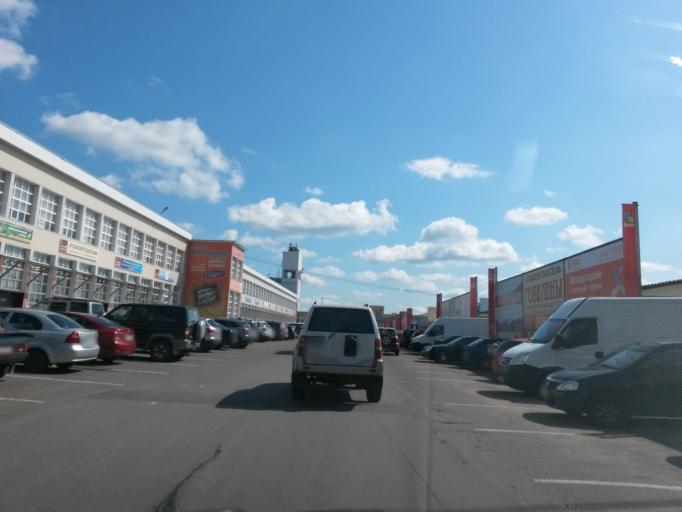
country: RU
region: Ivanovo
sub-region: Gorod Ivanovo
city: Ivanovo
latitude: 57.0107
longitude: 41.0054
